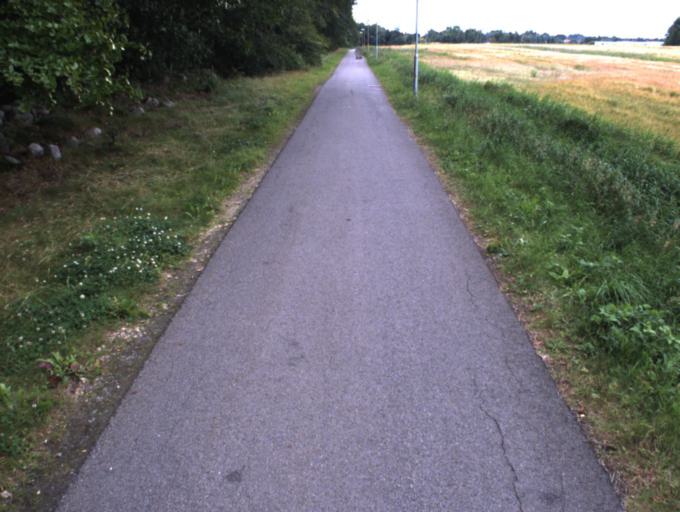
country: SE
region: Skane
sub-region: Helsingborg
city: Helsingborg
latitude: 56.0873
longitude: 12.6694
